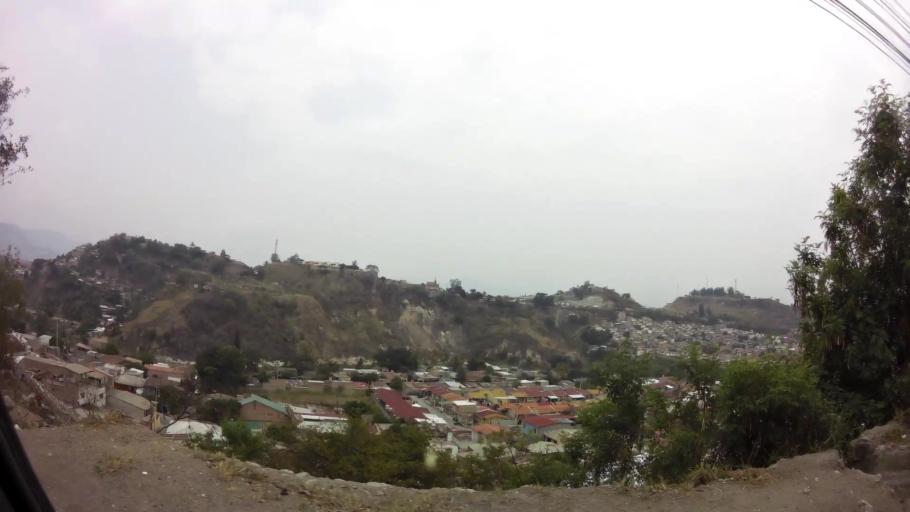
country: HN
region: Francisco Morazan
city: Tegucigalpa
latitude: 14.0786
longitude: -87.2259
